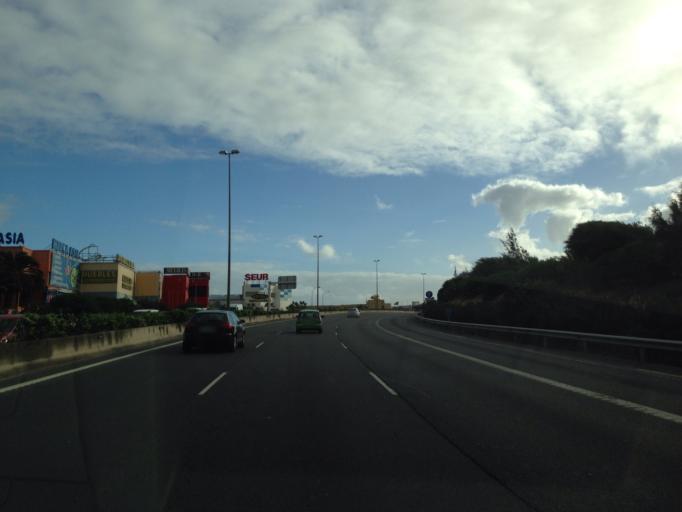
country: ES
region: Canary Islands
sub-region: Provincia de Las Palmas
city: Telde
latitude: 27.9789
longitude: -15.3910
